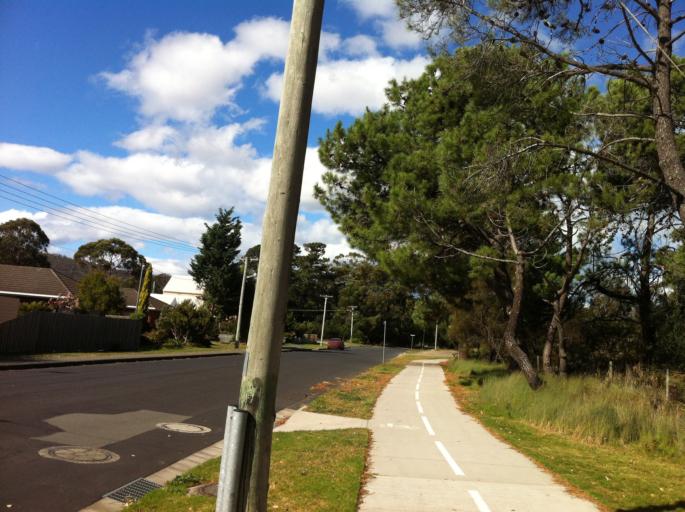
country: AU
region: Tasmania
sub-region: Clarence
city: Bellerive
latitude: -42.8786
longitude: 147.3810
